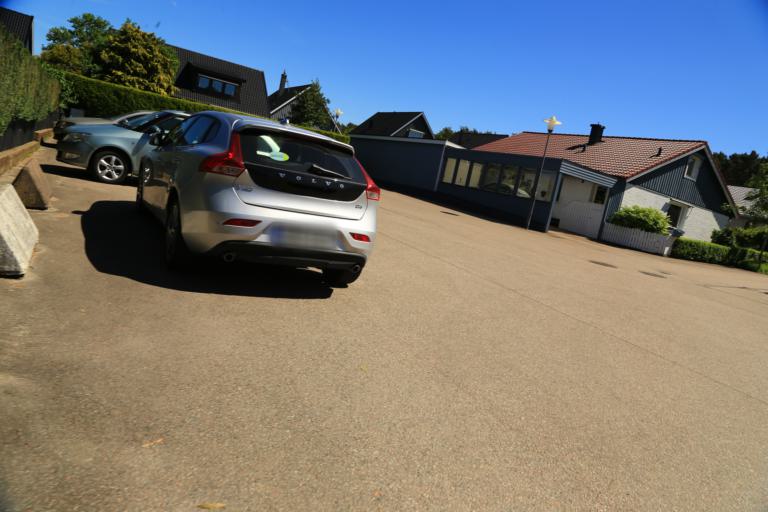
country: SE
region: Halland
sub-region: Varbergs Kommun
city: Varberg
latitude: 57.1096
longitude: 12.2843
